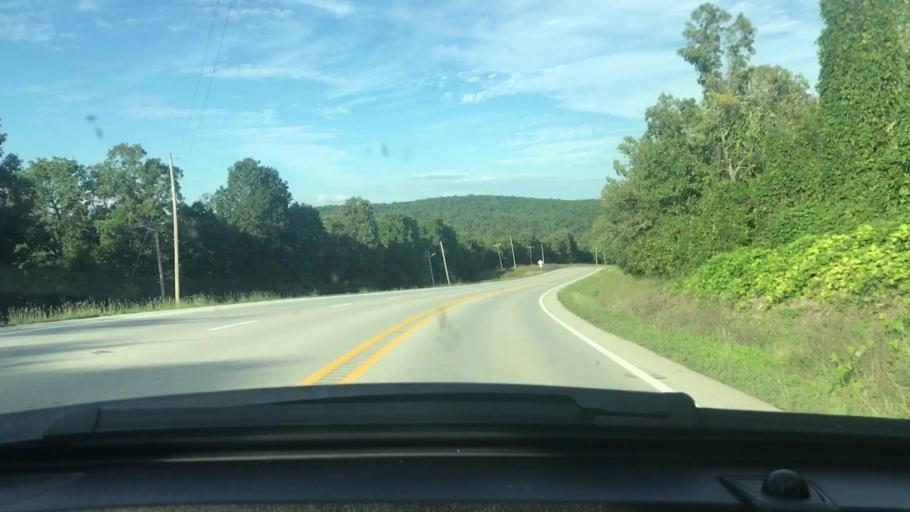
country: US
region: Arkansas
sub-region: Sharp County
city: Cherokee Village
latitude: 36.2734
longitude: -91.3654
